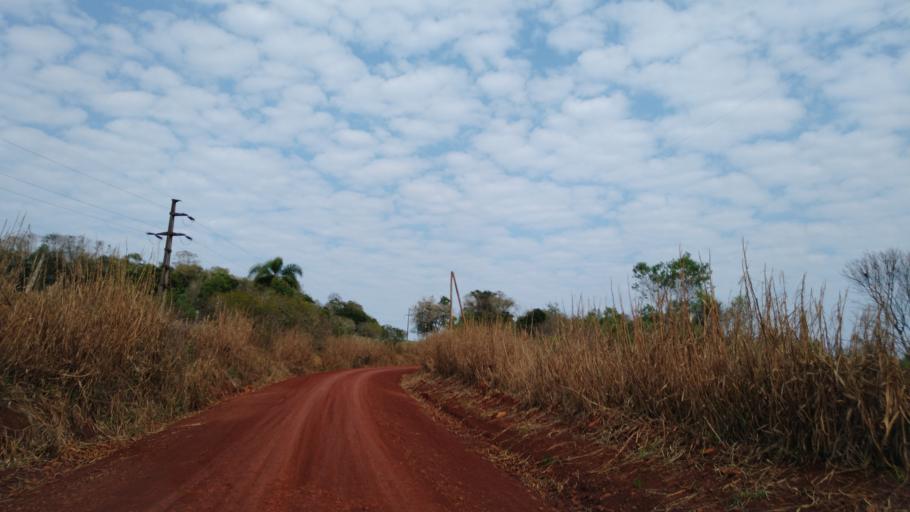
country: AR
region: Misiones
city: Capiovi
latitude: -26.9413
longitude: -55.0631
